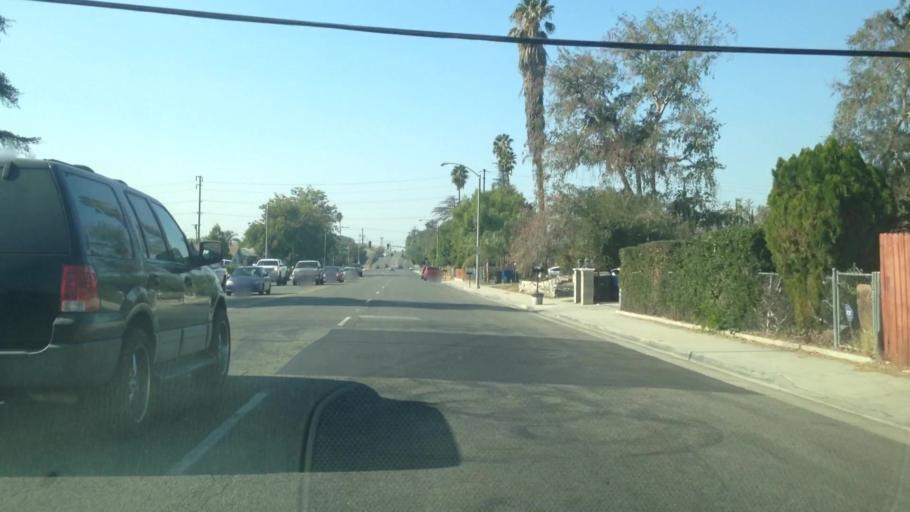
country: US
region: California
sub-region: Riverside County
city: Riverside
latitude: 33.9534
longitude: -117.4229
